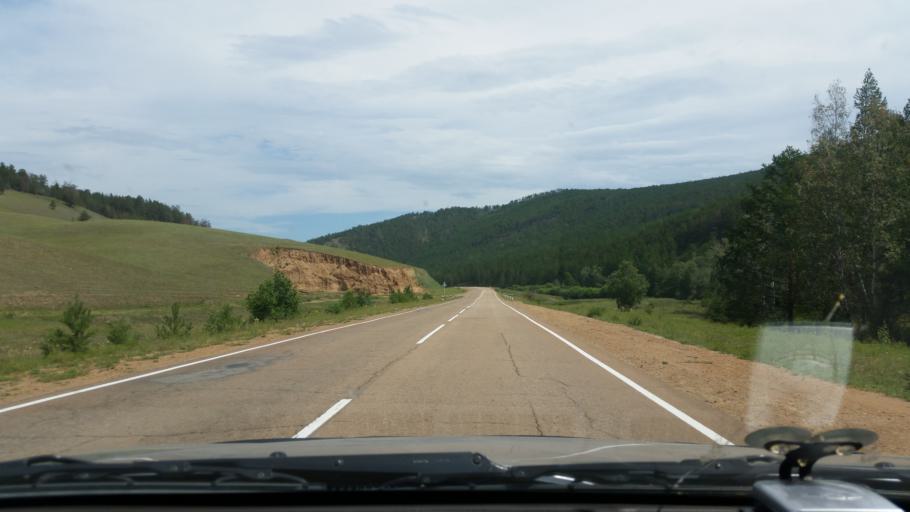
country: RU
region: Irkutsk
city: Yelantsy
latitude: 52.7738
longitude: 106.3653
